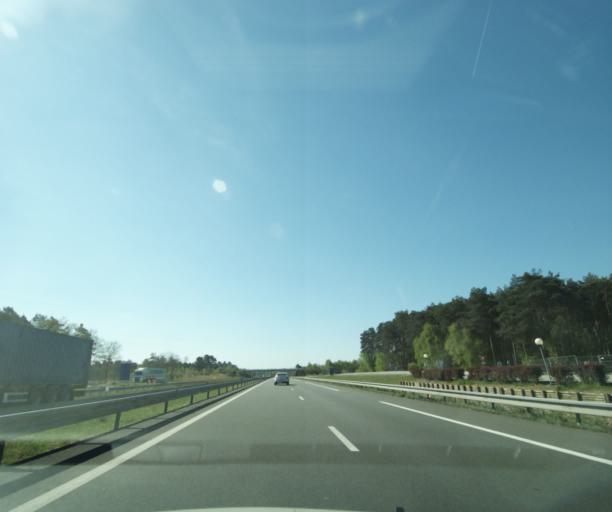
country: FR
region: Centre
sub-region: Departement du Loir-et-Cher
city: Theillay
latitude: 47.3481
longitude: 2.0492
